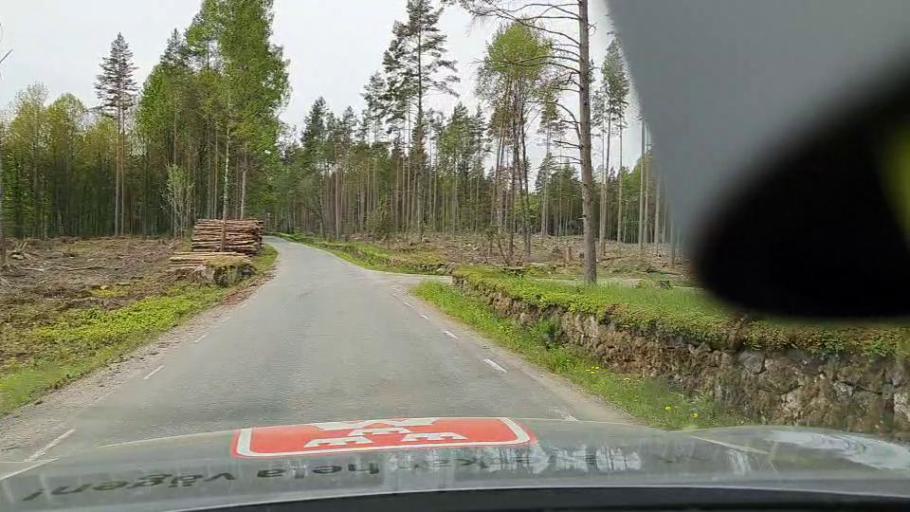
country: SE
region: Soedermanland
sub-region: Flens Kommun
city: Halleforsnas
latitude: 59.1023
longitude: 16.5101
